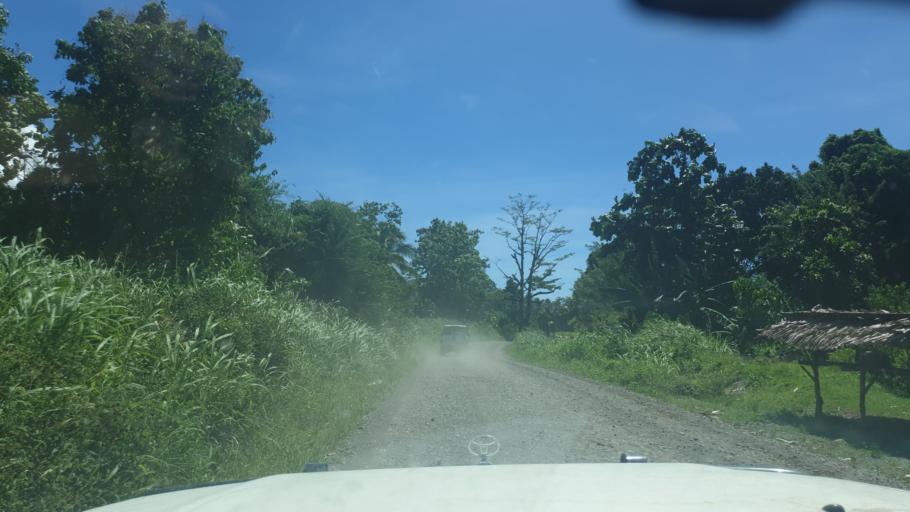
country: PG
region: Bougainville
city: Buka
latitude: -5.6627
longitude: 155.0976
